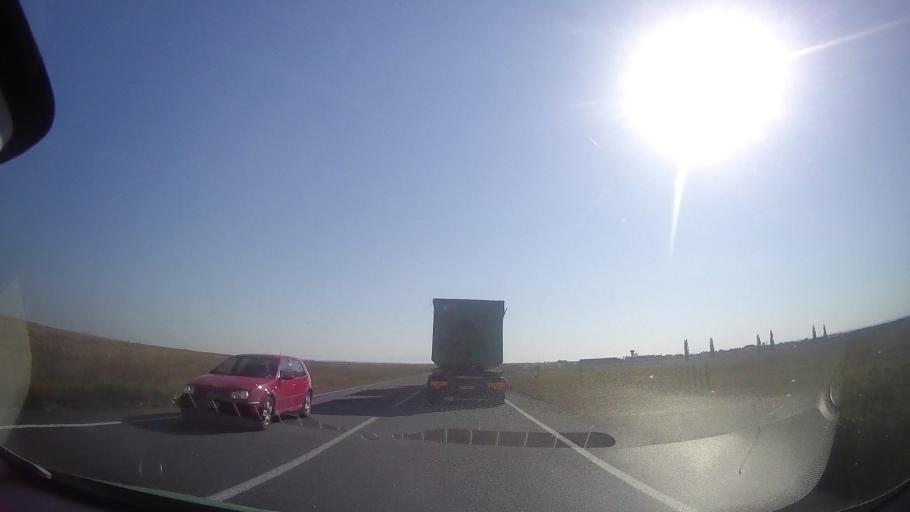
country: RO
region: Timis
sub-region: Comuna Ghizela
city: Ghizela
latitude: 45.7758
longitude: 21.6948
